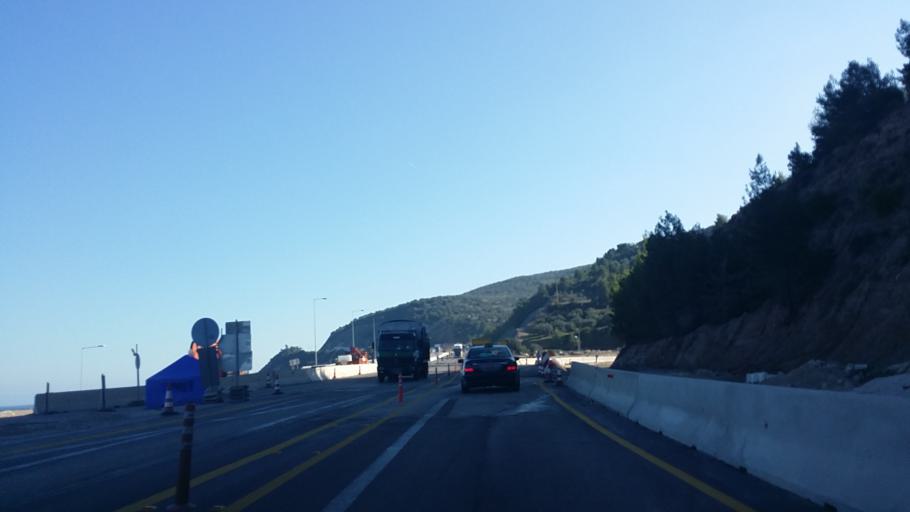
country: GR
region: West Greece
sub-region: Nomos Achaias
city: Akrata
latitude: 38.1767
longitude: 22.2368
